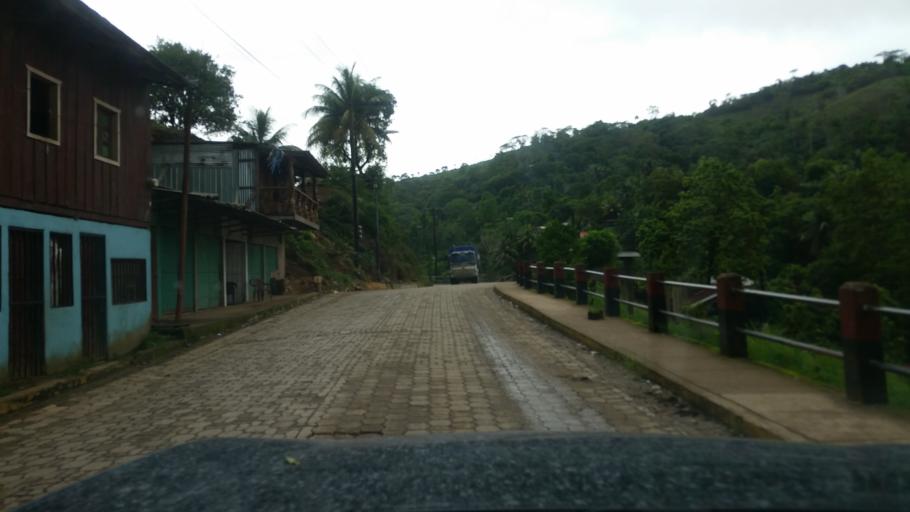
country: NI
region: Atlantico Norte (RAAN)
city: Bonanza
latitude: 14.0296
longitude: -84.6021
